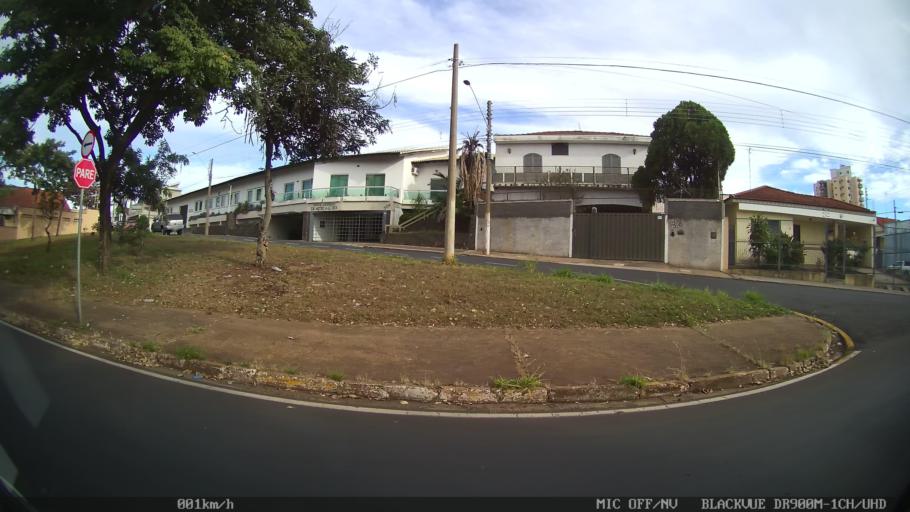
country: BR
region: Sao Paulo
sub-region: Catanduva
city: Catanduva
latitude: -21.1498
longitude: -48.9787
